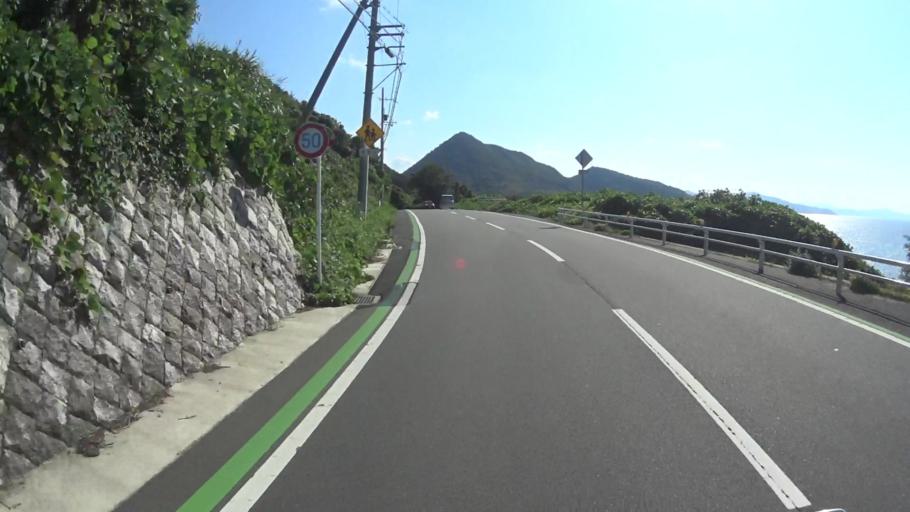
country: JP
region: Kyoto
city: Miyazu
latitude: 35.7271
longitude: 135.0866
